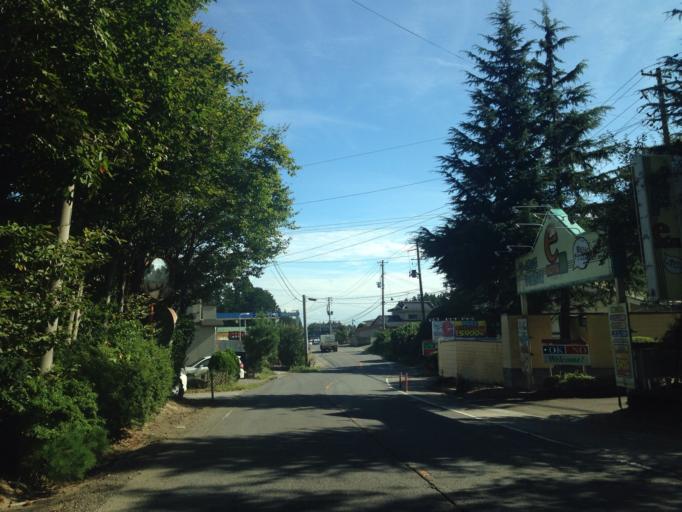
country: JP
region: Fukushima
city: Motomiya
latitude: 37.5579
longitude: 140.3544
